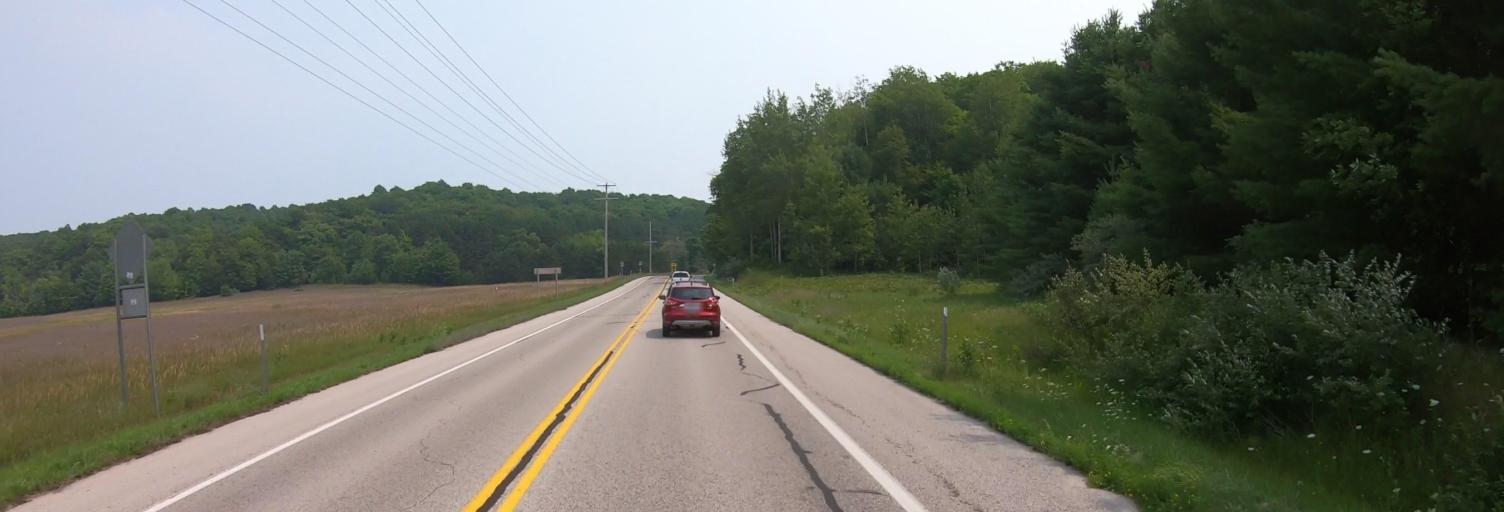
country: US
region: Michigan
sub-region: Leelanau County
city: Leland
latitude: 45.0991
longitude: -85.6566
